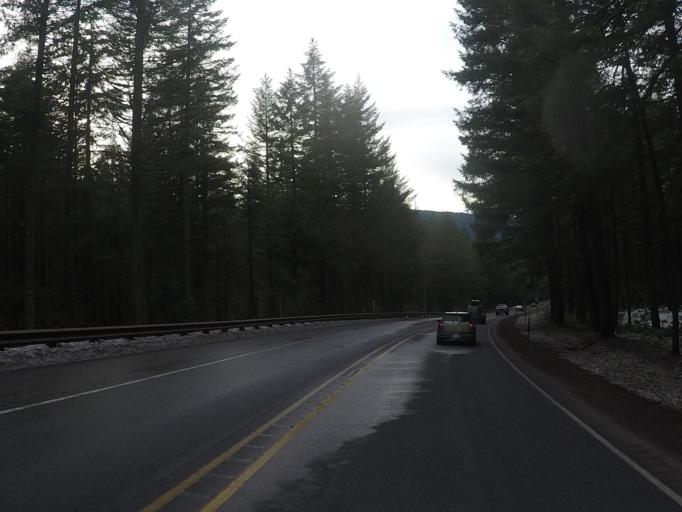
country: US
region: Oregon
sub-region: Clackamas County
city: Mount Hood Village
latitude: 45.3051
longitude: -121.8704
